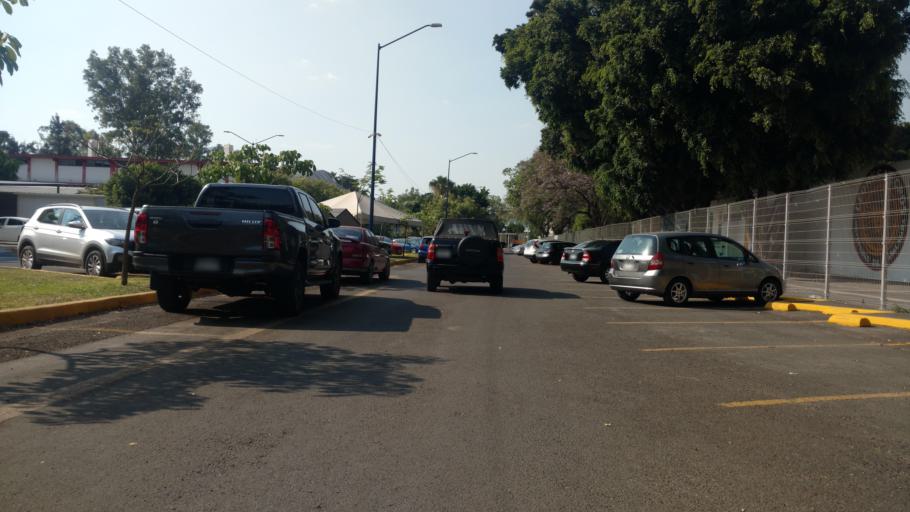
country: MX
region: Jalisco
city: Tlaquepaque
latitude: 20.6570
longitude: -103.3240
